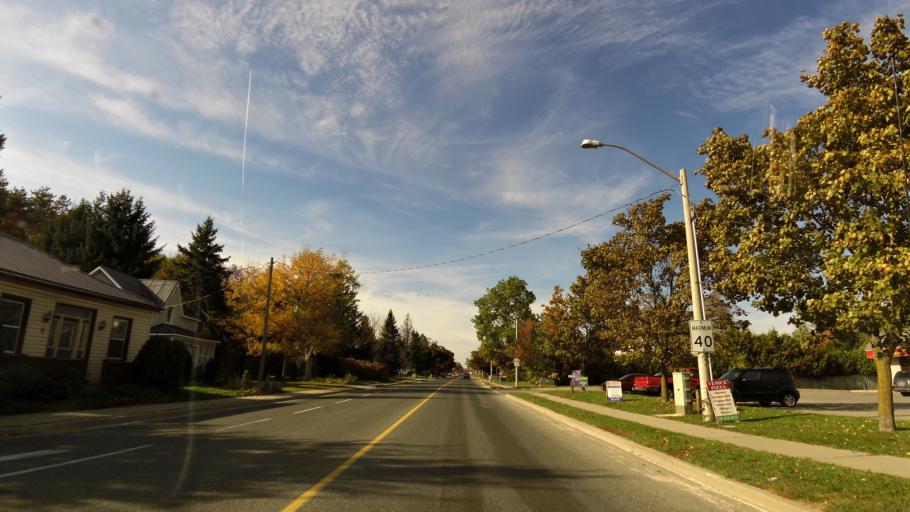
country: CA
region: Ontario
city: Orangeville
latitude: 43.7662
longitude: -80.0586
